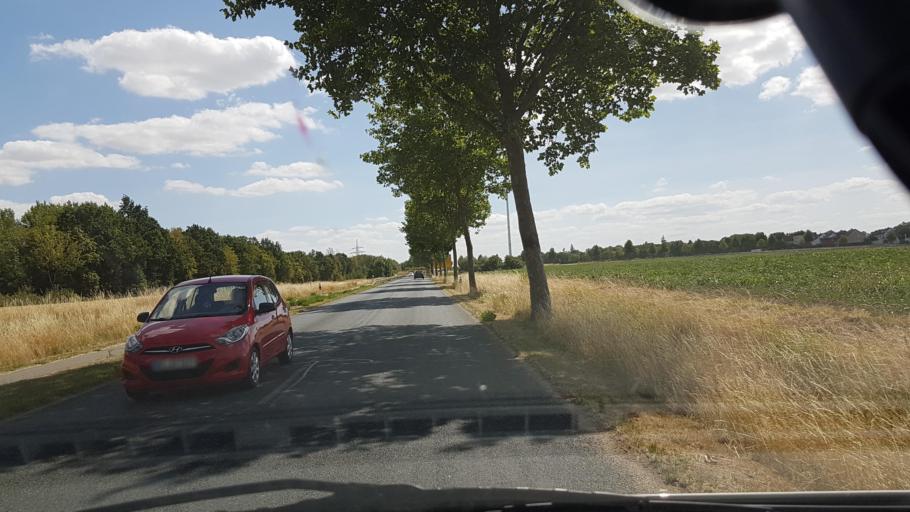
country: DE
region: Lower Saxony
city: Schoningen
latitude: 52.1529
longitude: 10.9713
